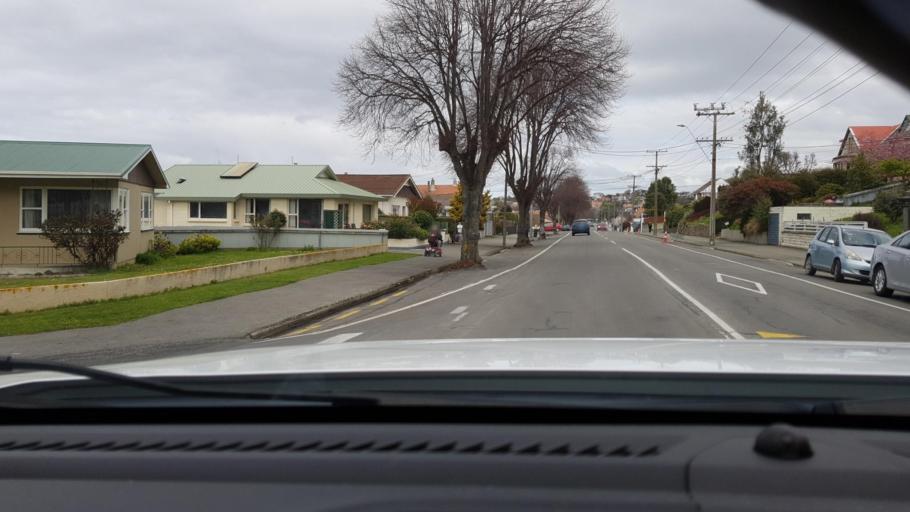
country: NZ
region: Otago
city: Oamaru
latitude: -45.0926
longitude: 170.9702
